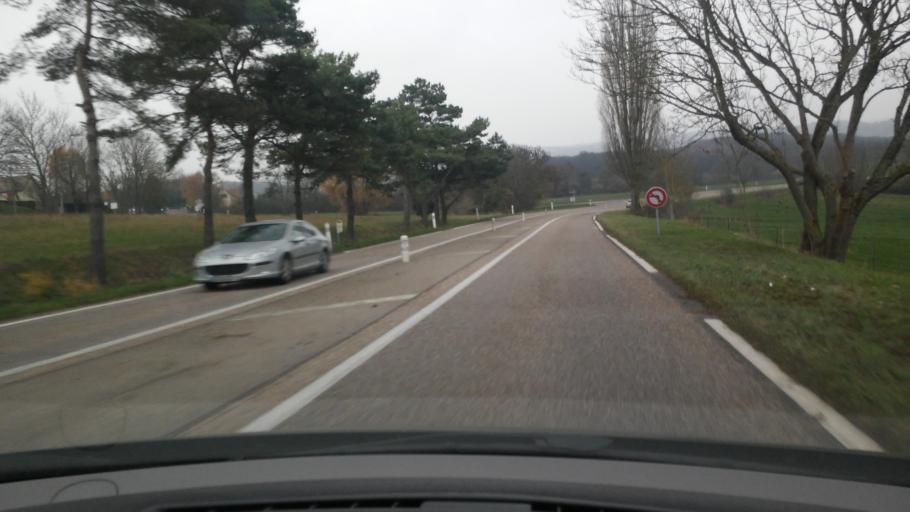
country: FR
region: Lorraine
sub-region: Departement de la Moselle
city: Courcelles-Chaussy
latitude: 49.1156
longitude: 6.3608
